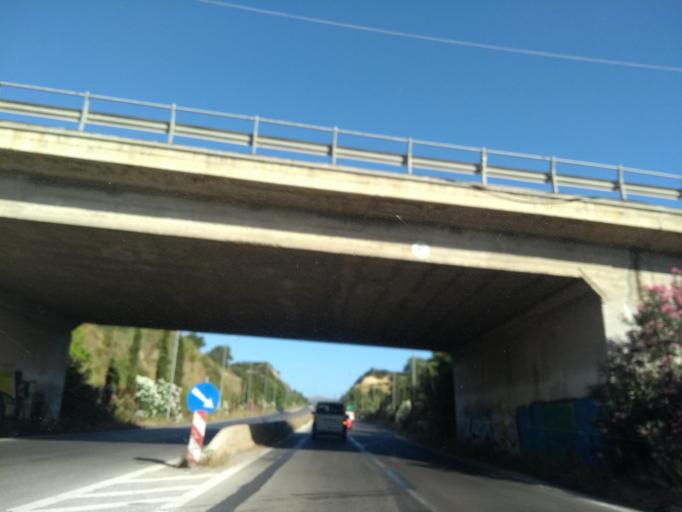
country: GR
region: Crete
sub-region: Nomos Chanias
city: Kolympari
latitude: 35.5191
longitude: 23.8201
